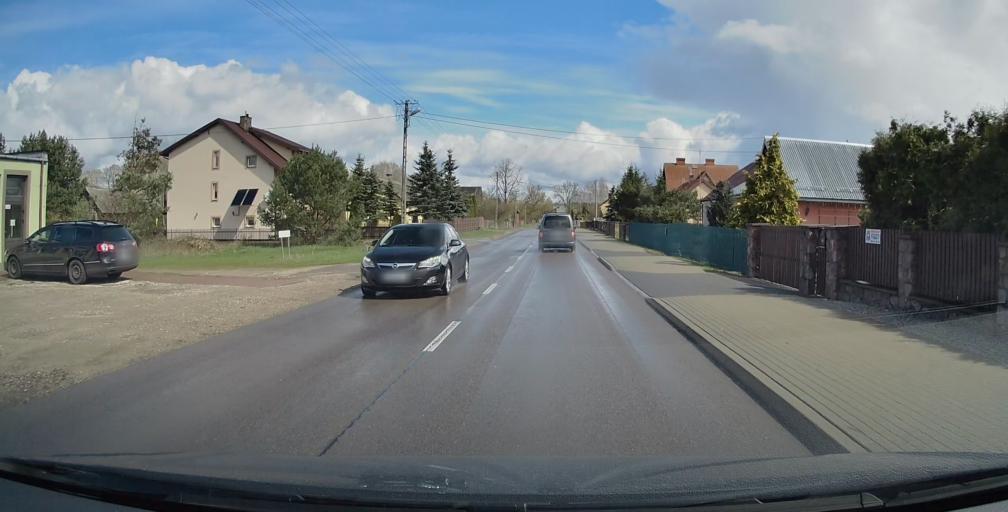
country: PL
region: Masovian Voivodeship
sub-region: Powiat wyszkowski
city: Dlugosiodlo
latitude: 52.6967
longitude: 21.6025
